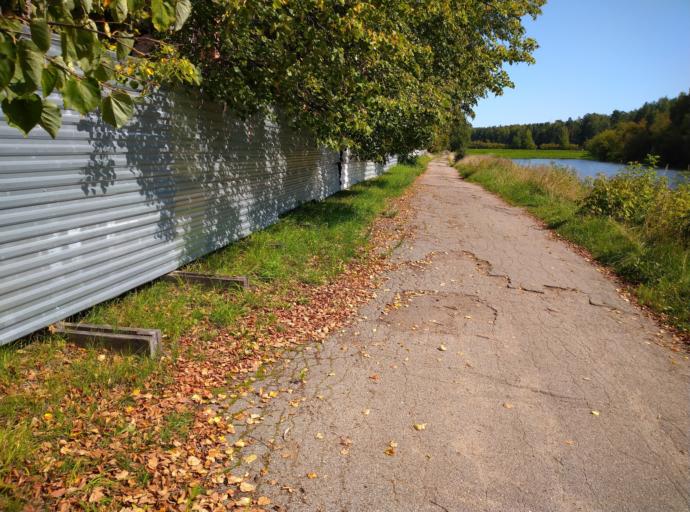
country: RU
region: Kostroma
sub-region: Kostromskoy Rayon
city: Kostroma
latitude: 57.7983
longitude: 40.9549
